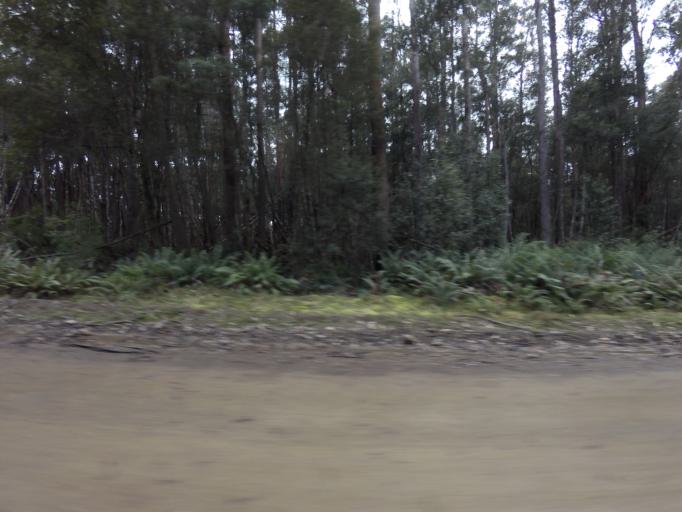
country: AU
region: Tasmania
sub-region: Huon Valley
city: Geeveston
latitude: -43.4809
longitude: 146.8911
